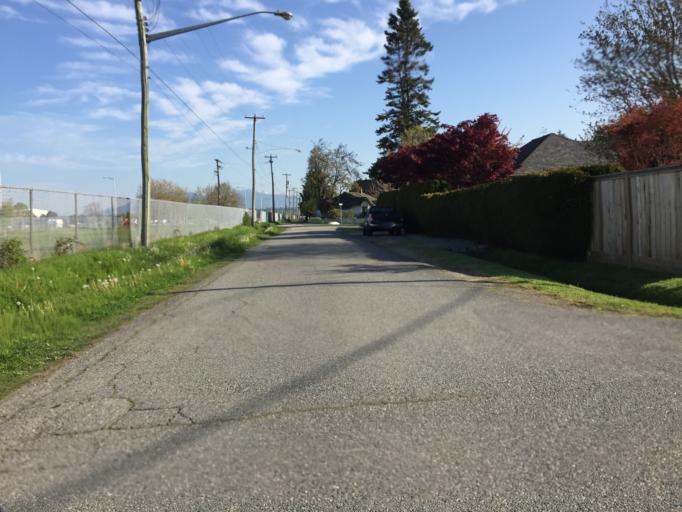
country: CA
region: British Columbia
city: Richmond
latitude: 49.1873
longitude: -123.1504
